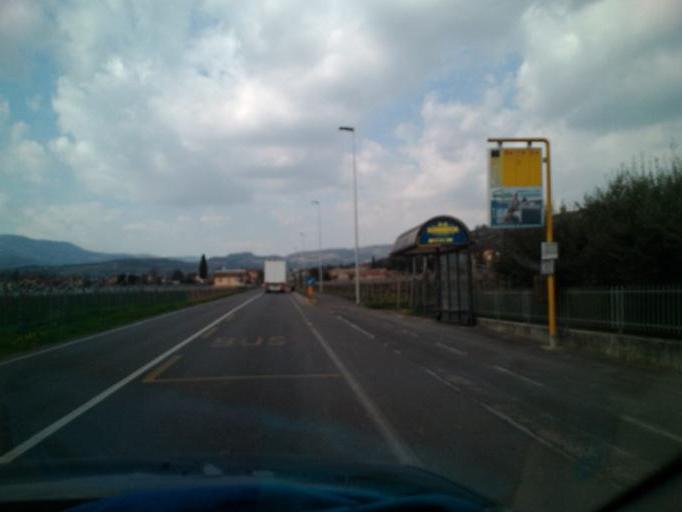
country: IT
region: Veneto
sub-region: Provincia di Verona
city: Pedemonte
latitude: 45.5115
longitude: 10.9137
